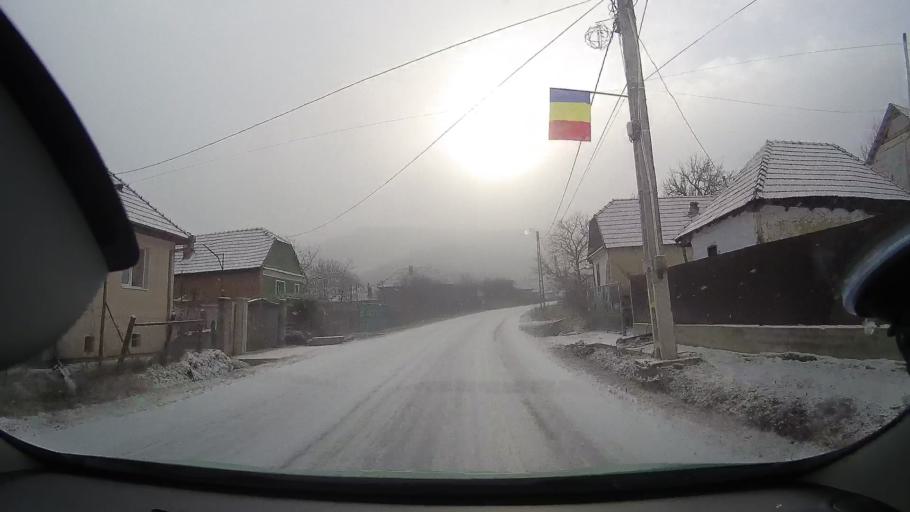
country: RO
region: Alba
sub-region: Comuna Rimetea
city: Rimetea
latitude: 46.3917
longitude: 23.5618
